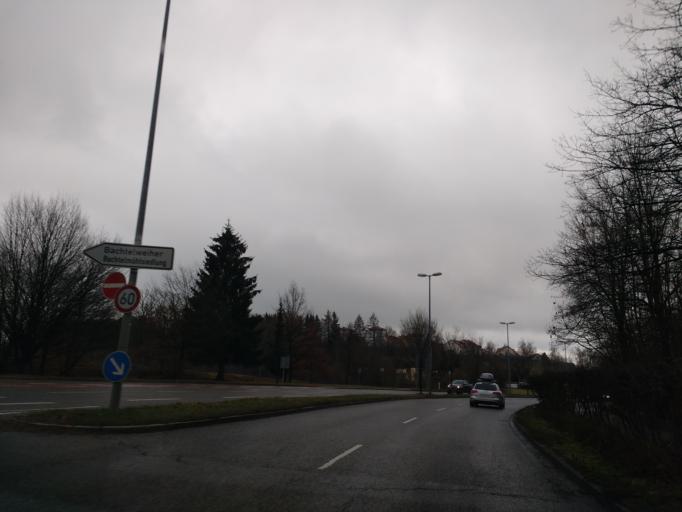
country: DE
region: Bavaria
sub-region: Swabia
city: Kempten (Allgaeu)
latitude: 47.7236
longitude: 10.3336
